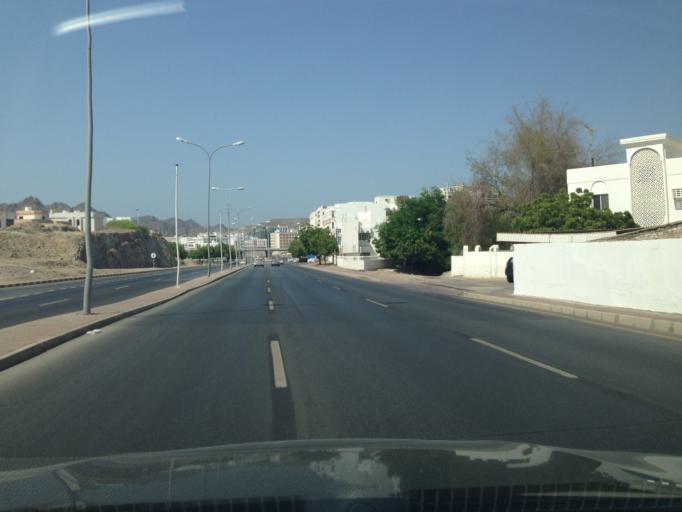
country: OM
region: Muhafazat Masqat
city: Muscat
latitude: 23.6117
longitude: 58.5412
